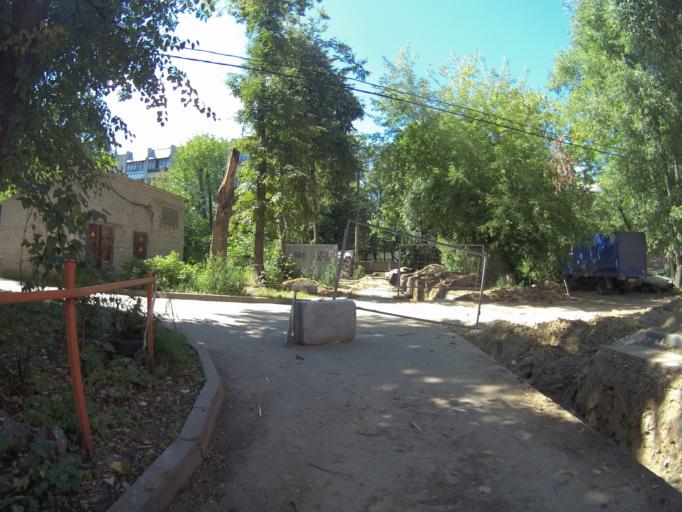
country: RU
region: Vladimir
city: Vladimir
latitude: 56.1327
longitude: 40.3706
